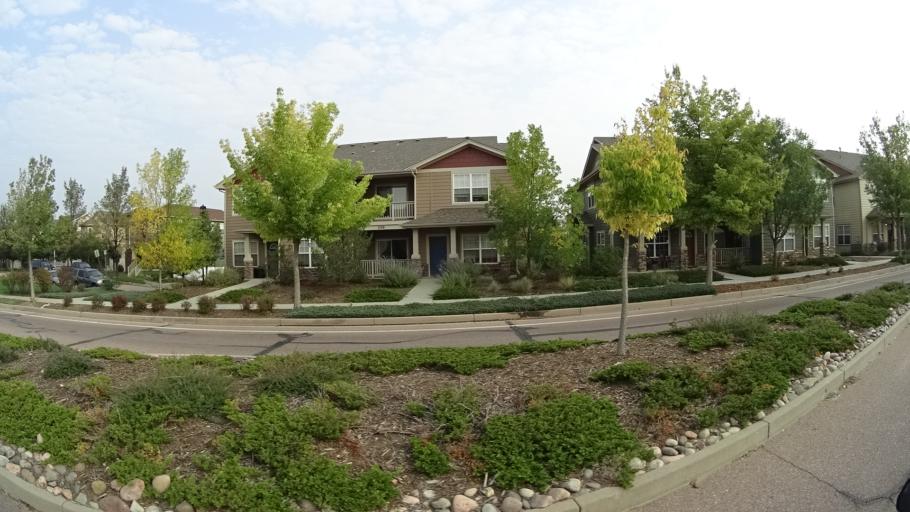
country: US
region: Colorado
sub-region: El Paso County
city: Stratmoor
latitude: 38.8080
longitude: -104.7850
